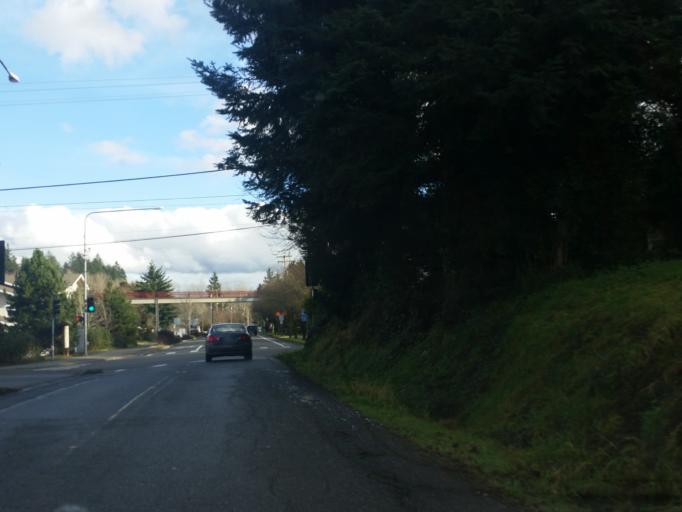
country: US
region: Washington
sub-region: King County
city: Bothell
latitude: 47.7566
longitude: -122.2045
